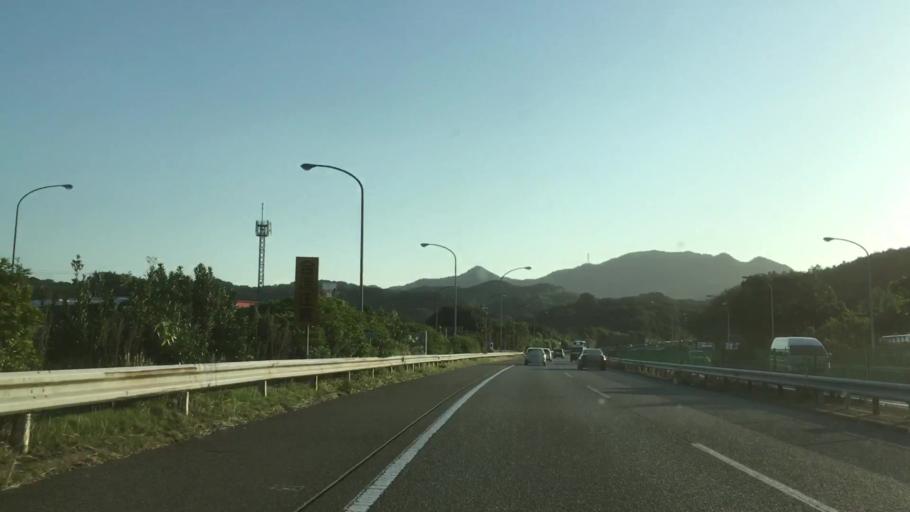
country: JP
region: Yamaguchi
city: Shimonoseki
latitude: 34.0511
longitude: 131.0049
